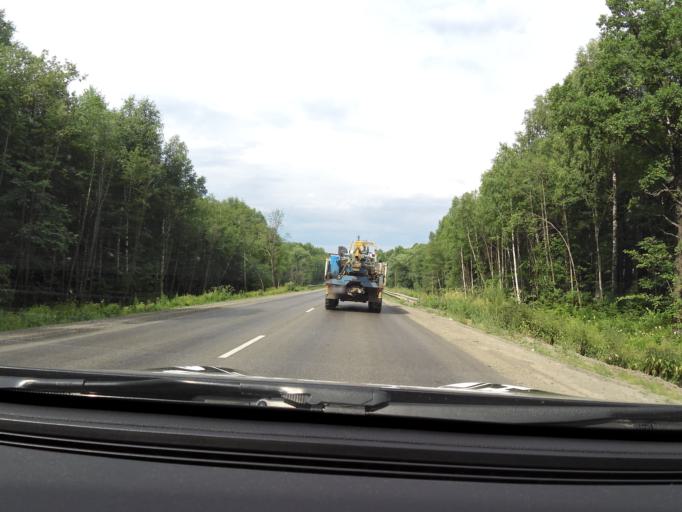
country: RU
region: Chelyabinsk
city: Asha
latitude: 54.8820
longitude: 57.2551
